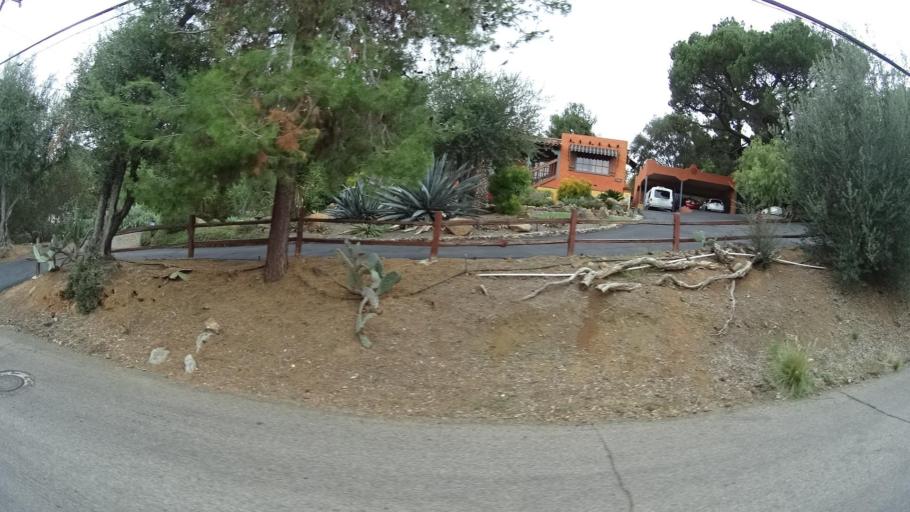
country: US
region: California
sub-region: San Diego County
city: Spring Valley
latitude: 32.7465
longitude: -117.0060
